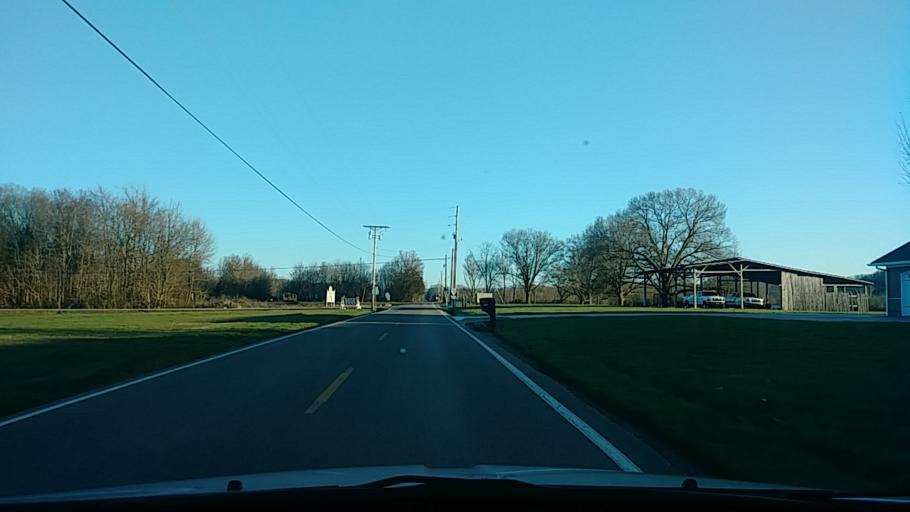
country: US
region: Tennessee
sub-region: Jefferson County
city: White Pine
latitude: 36.1463
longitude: -83.1471
